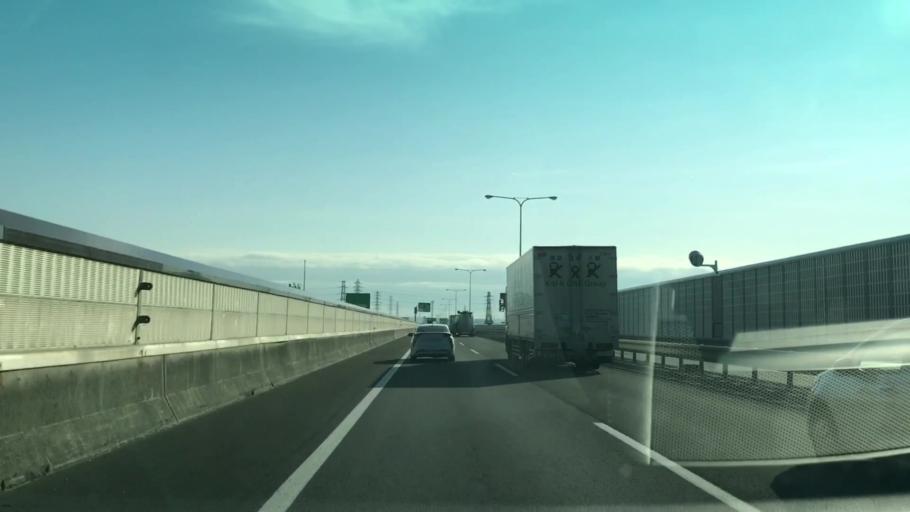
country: JP
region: Hokkaido
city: Sapporo
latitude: 43.0963
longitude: 141.3966
